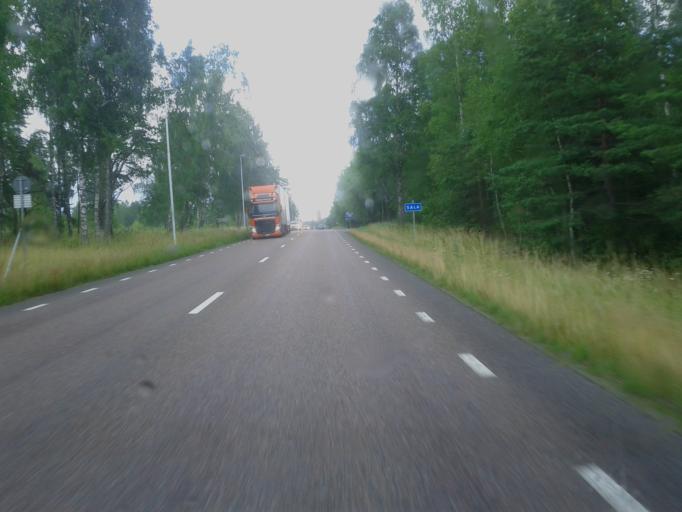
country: SE
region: Vaestmanland
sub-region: Sala Kommun
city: Sala
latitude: 59.9030
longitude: 16.5781
